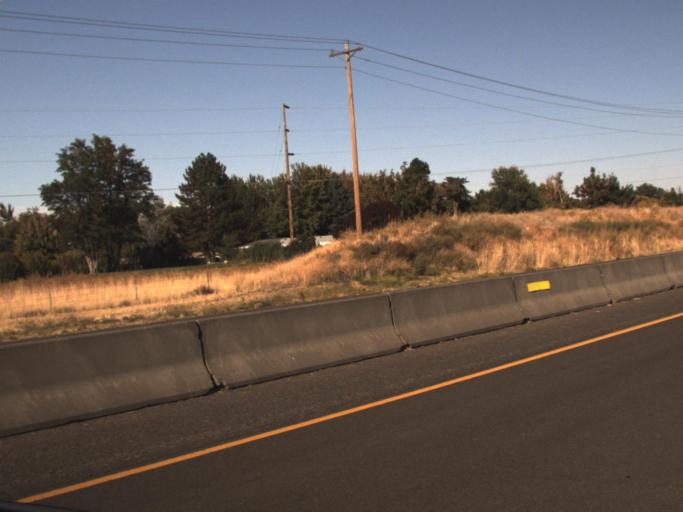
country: US
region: Washington
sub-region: Walla Walla County
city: College Place
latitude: 46.0340
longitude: -118.3765
